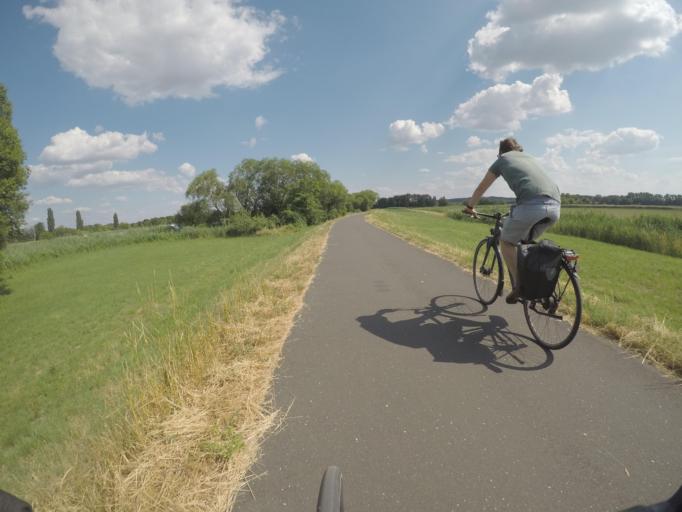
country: DE
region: Brandenburg
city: Ketzin
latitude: 52.4462
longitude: 12.8742
